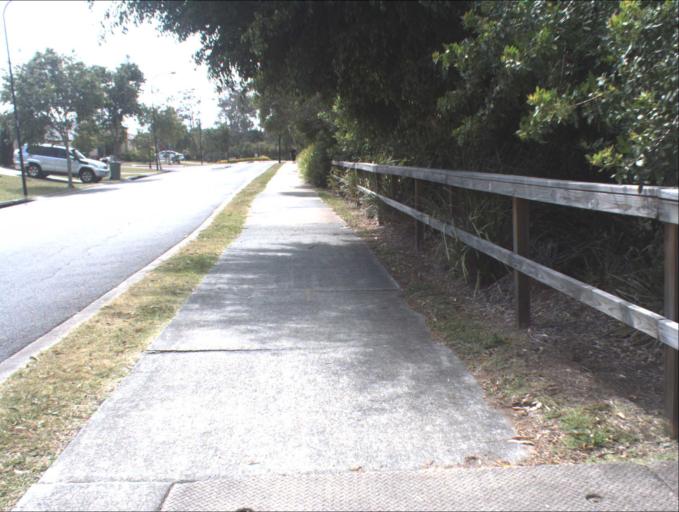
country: AU
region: Queensland
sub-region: Logan
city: Woodridge
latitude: -27.6162
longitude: 153.1058
